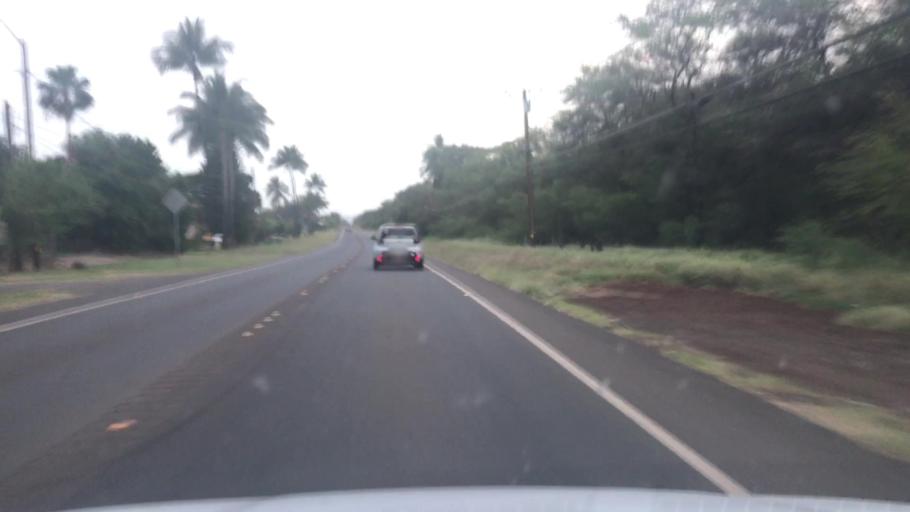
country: US
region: Hawaii
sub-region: Maui County
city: Kaunakakai
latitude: 21.0690
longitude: -156.9620
